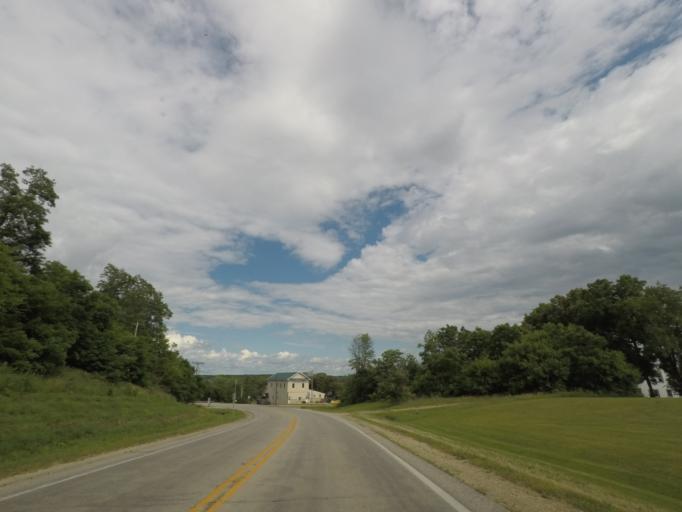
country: US
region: Wisconsin
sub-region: Dane County
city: Belleville
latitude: 42.8274
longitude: -89.5126
